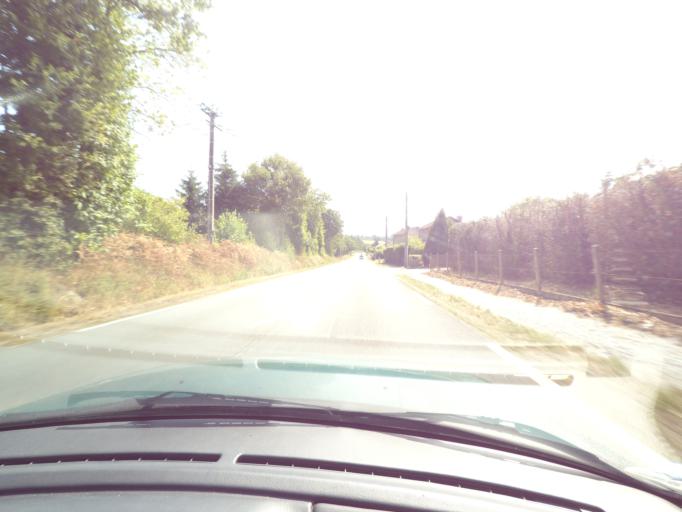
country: FR
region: Limousin
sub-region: Departement de la Haute-Vienne
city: Feytiat
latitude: 45.8081
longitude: 1.3516
